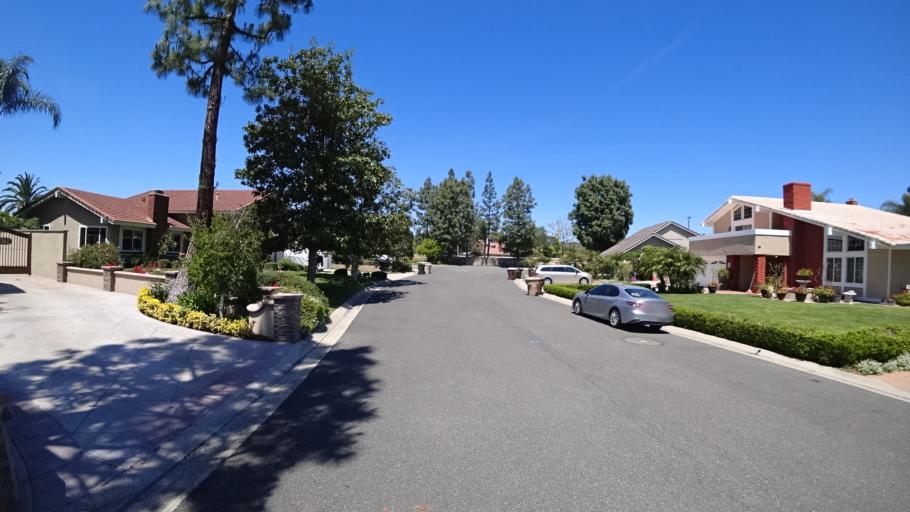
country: US
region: California
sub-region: Orange County
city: Villa Park
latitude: 33.8099
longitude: -117.8119
